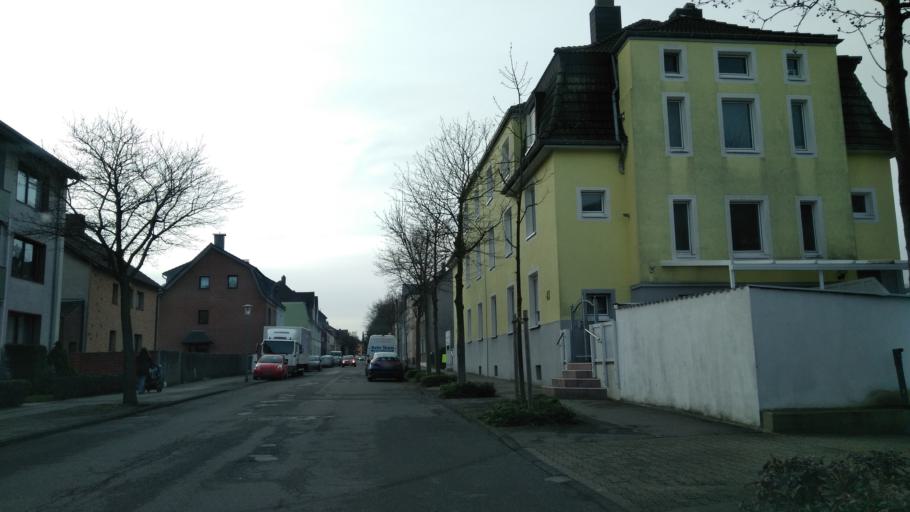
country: DE
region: North Rhine-Westphalia
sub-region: Regierungsbezirk Munster
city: Gladbeck
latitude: 51.5841
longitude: 6.9979
